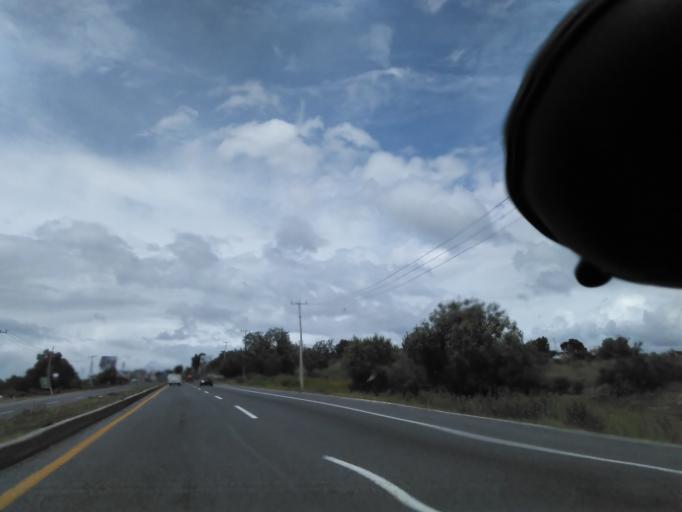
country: MX
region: Hidalgo
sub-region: Atotonilco de Tula
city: Paseos de la Pradera
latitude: 19.9270
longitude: -99.2368
